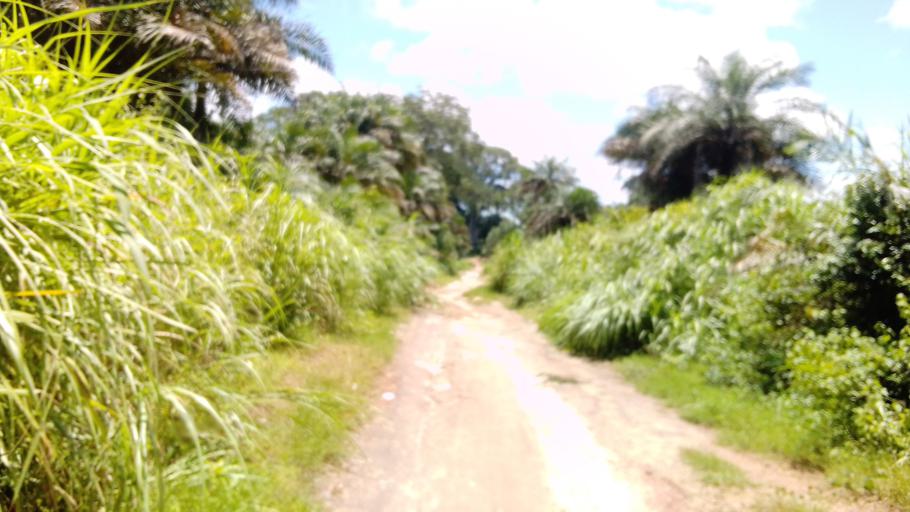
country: SL
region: Northern Province
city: Makeni
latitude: 9.0369
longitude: -12.1591
